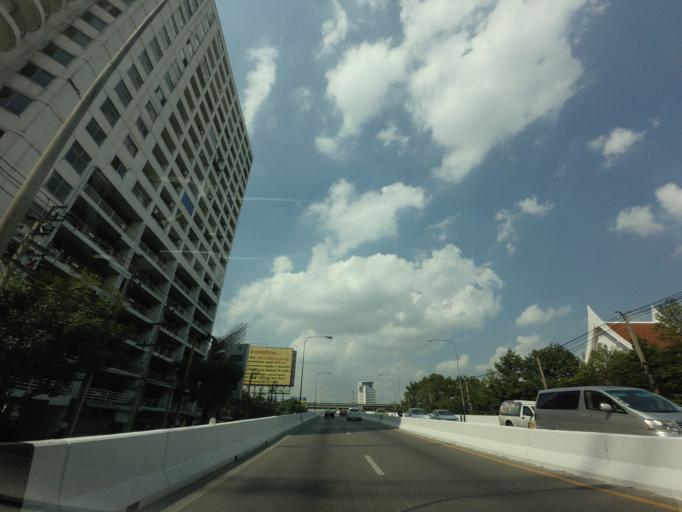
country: TH
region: Bangkok
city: Chatuchak
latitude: 13.8464
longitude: 100.5635
